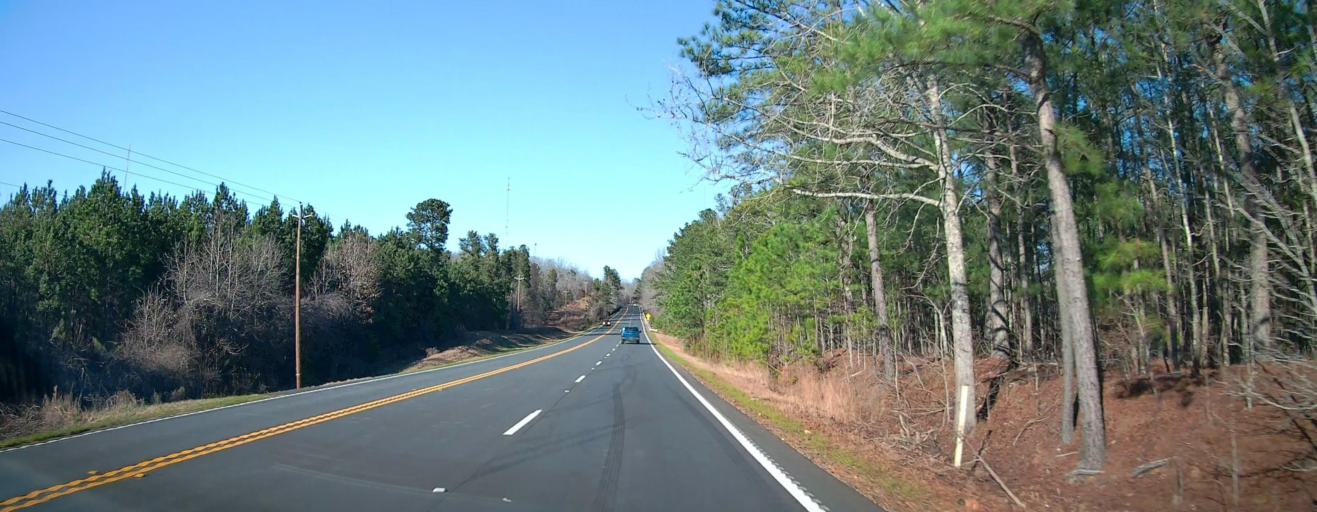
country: US
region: Georgia
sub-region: Talbot County
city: Sardis
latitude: 32.8390
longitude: -84.6964
